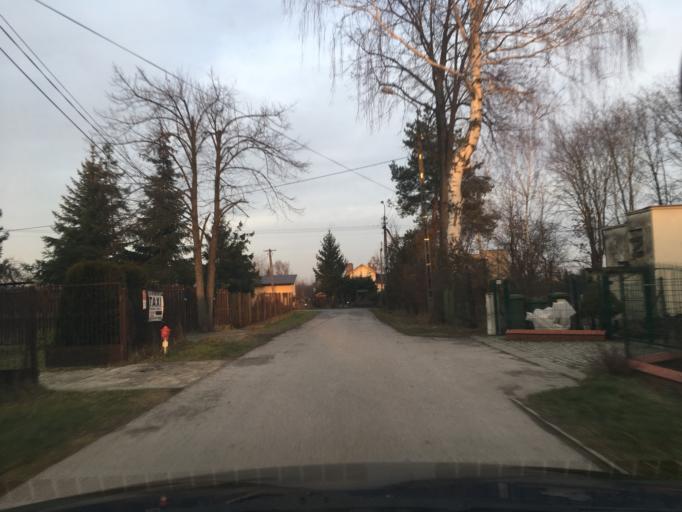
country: PL
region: Masovian Voivodeship
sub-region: Powiat piaseczynski
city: Lesznowola
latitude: 52.0378
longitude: 20.9622
